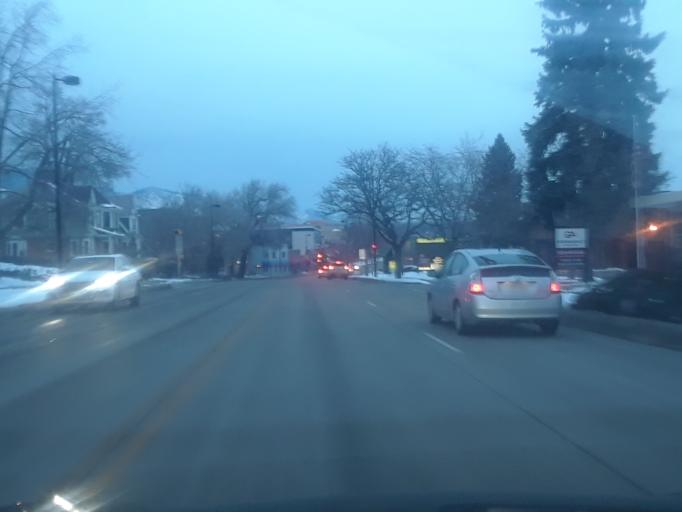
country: US
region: Colorado
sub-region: Boulder County
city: Boulder
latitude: 40.0226
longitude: -105.2816
